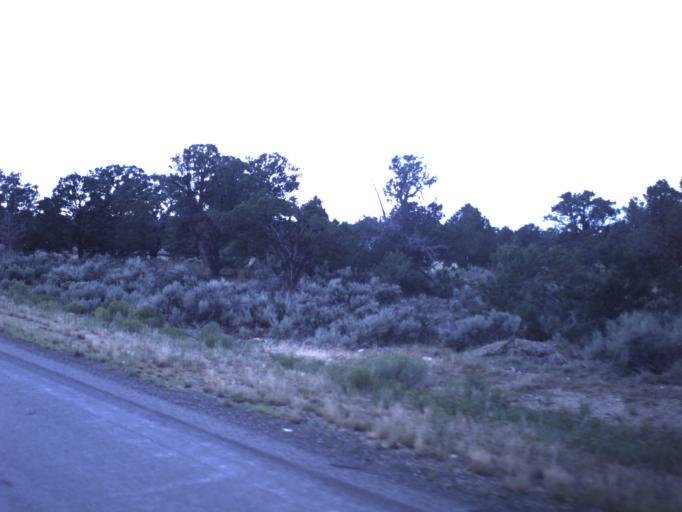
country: US
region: Utah
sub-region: Duchesne County
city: Duchesne
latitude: 40.1813
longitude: -110.6393
